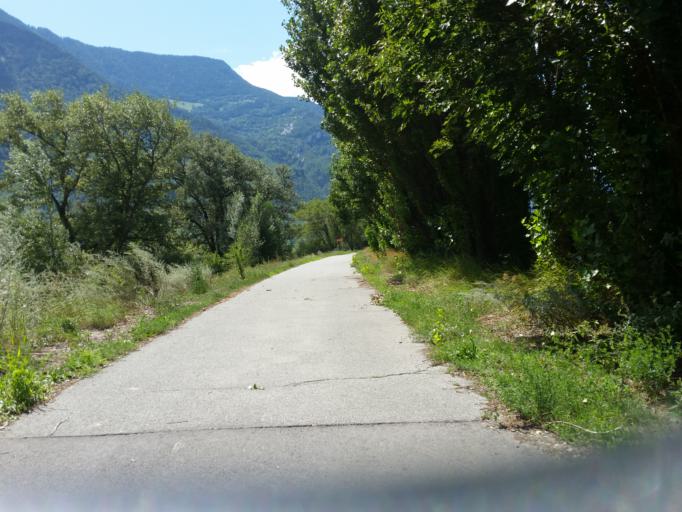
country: CH
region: Valais
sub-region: Martigny District
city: Saillon
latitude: 46.1643
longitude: 7.1971
